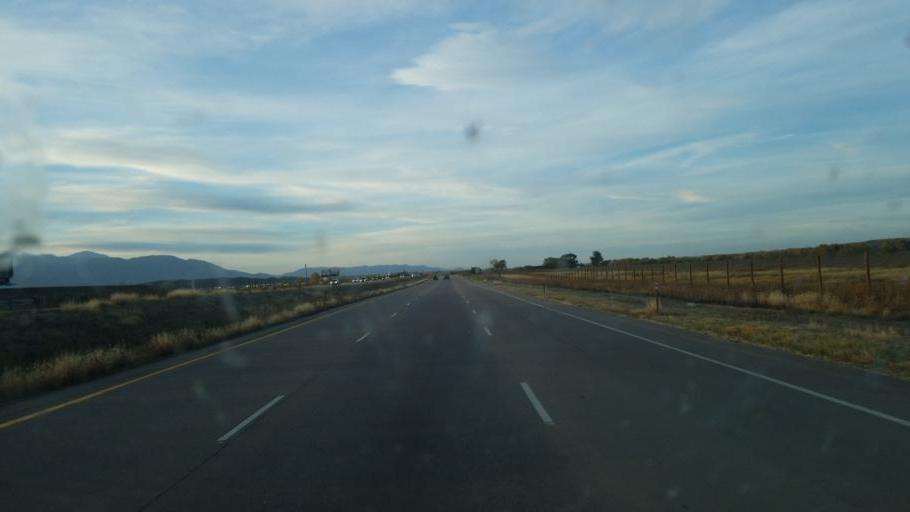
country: US
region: Colorado
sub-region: El Paso County
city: Fountain
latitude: 38.5927
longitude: -104.6723
